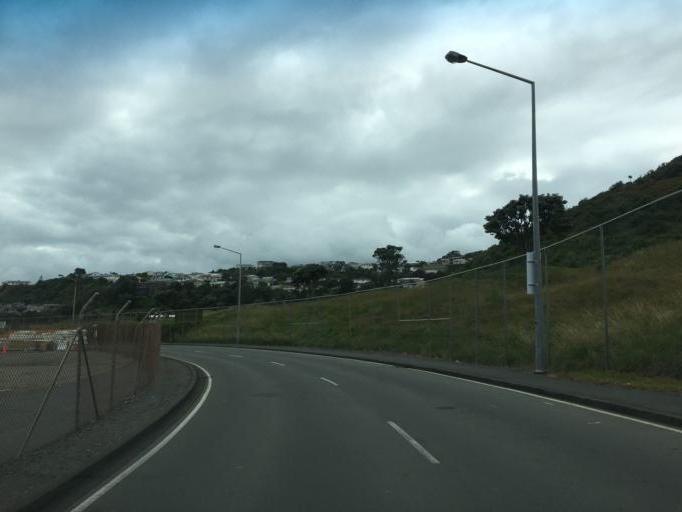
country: NZ
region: Wellington
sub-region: Wellington City
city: Wellington
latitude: -41.3343
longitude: 174.8117
